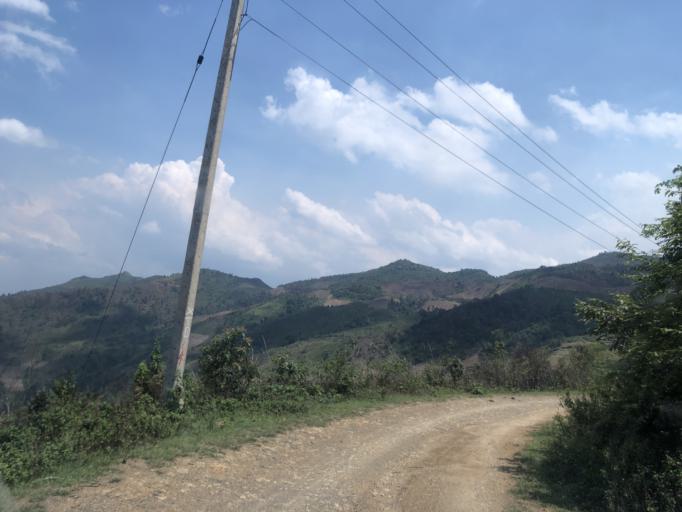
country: LA
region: Phongsali
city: Phongsali
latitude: 21.3974
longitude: 102.2243
